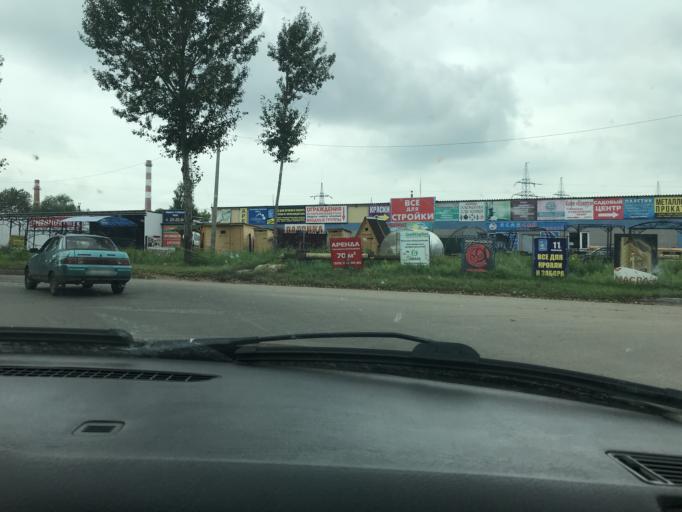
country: RU
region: Kaluga
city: Kaluga
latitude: 54.5343
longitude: 36.2952
